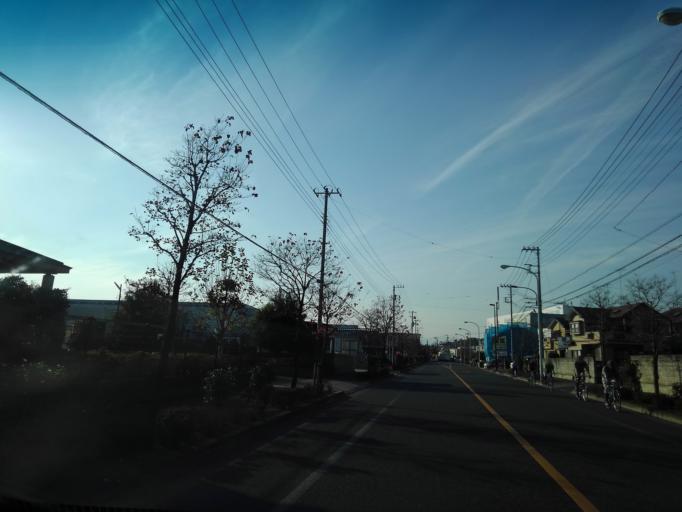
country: JP
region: Tokyo
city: Fussa
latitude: 35.7929
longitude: 139.3514
